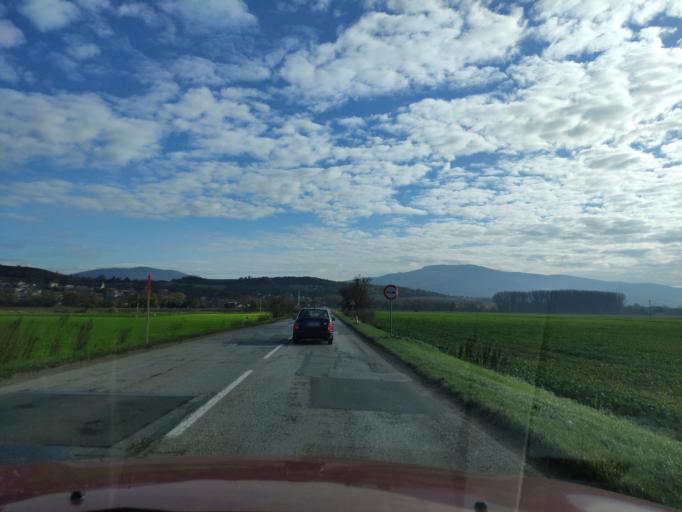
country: SK
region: Kosicky
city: Kosice
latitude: 48.6603
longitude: 21.3465
